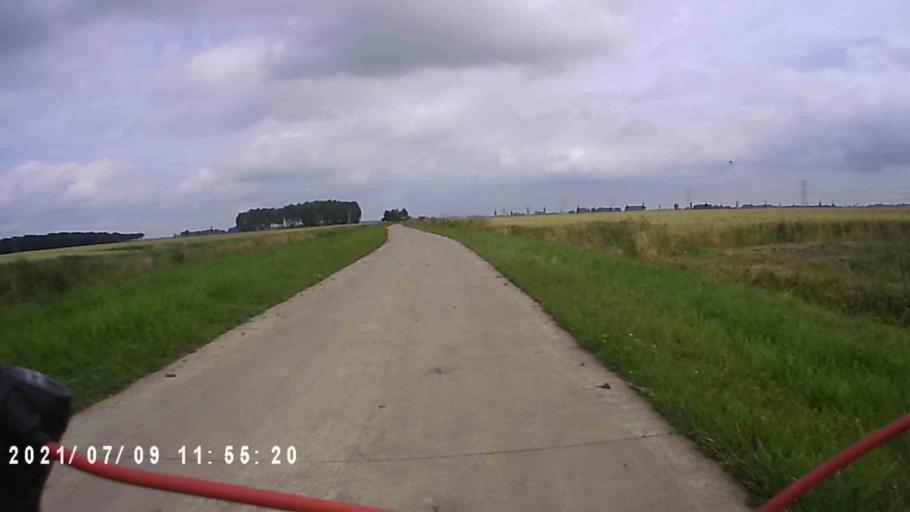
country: NL
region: Groningen
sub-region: Gemeente Veendam
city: Veendam
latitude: 53.1879
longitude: 6.9038
